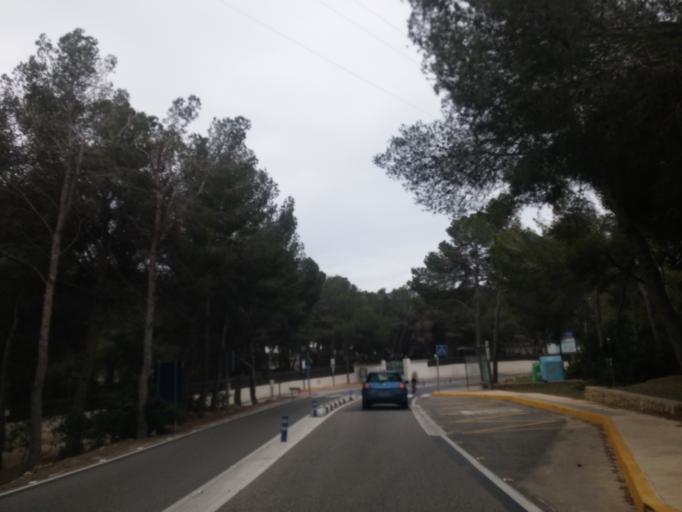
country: ES
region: Valencia
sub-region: Provincia de Alicante
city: Moraira
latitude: 38.6697
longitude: 0.0921
